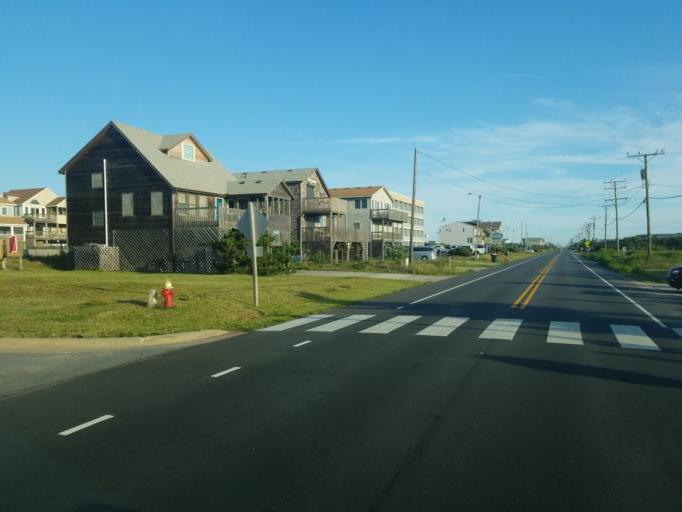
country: US
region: North Carolina
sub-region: Dare County
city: Kill Devil Hills
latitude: 36.0185
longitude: -75.6600
